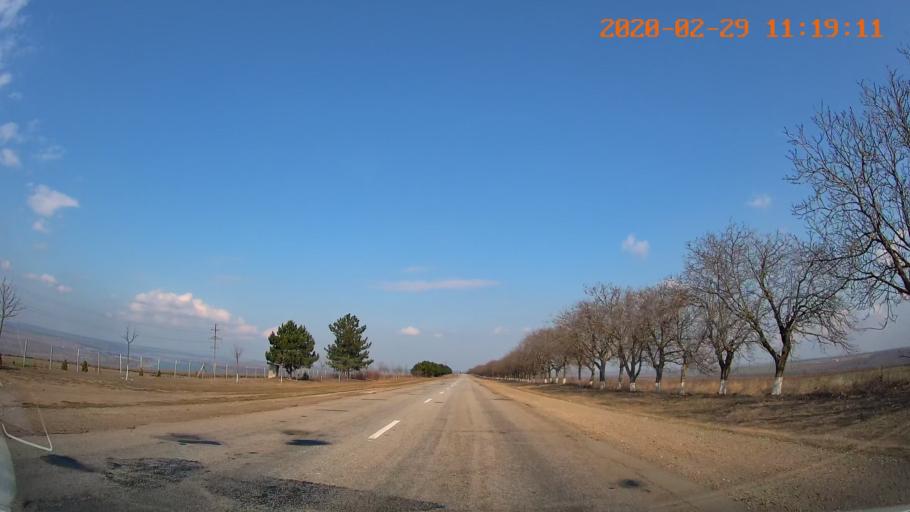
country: MD
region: Telenesti
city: Cocieri
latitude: 47.3460
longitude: 29.1755
